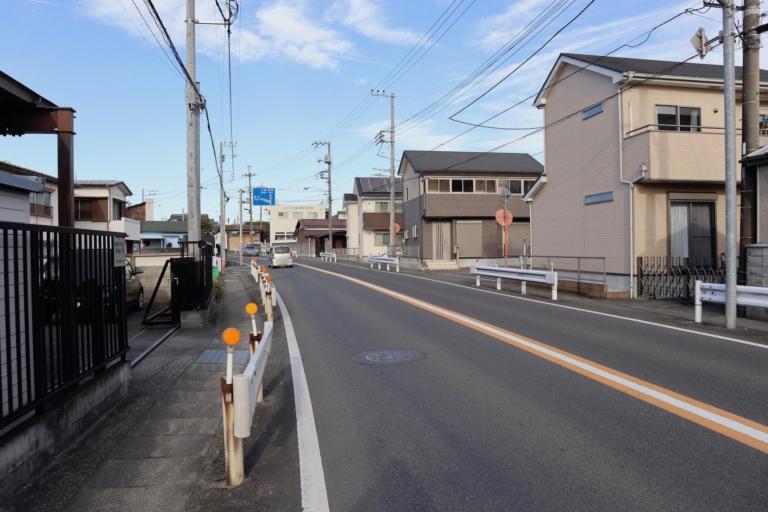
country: JP
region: Tokyo
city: Fussa
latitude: 35.7098
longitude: 139.3381
